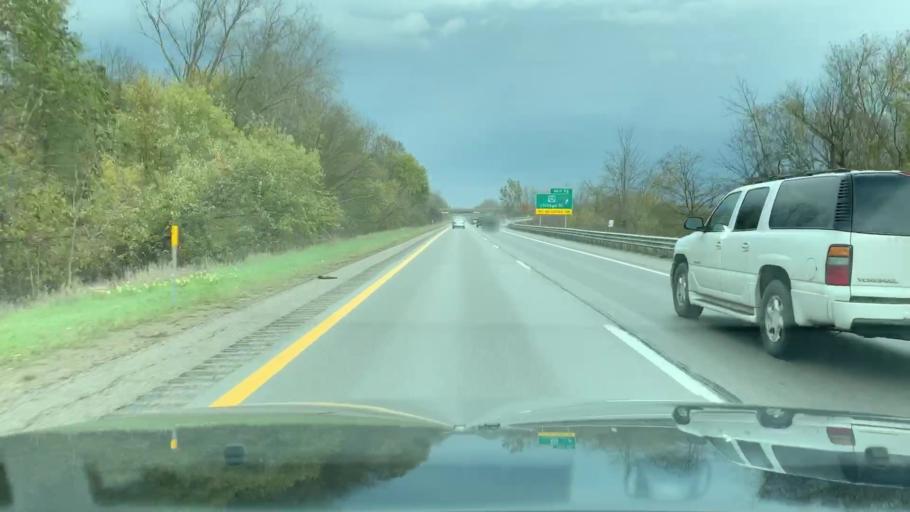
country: US
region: Michigan
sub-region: Kent County
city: Grandville
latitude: 42.9291
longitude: -85.7390
